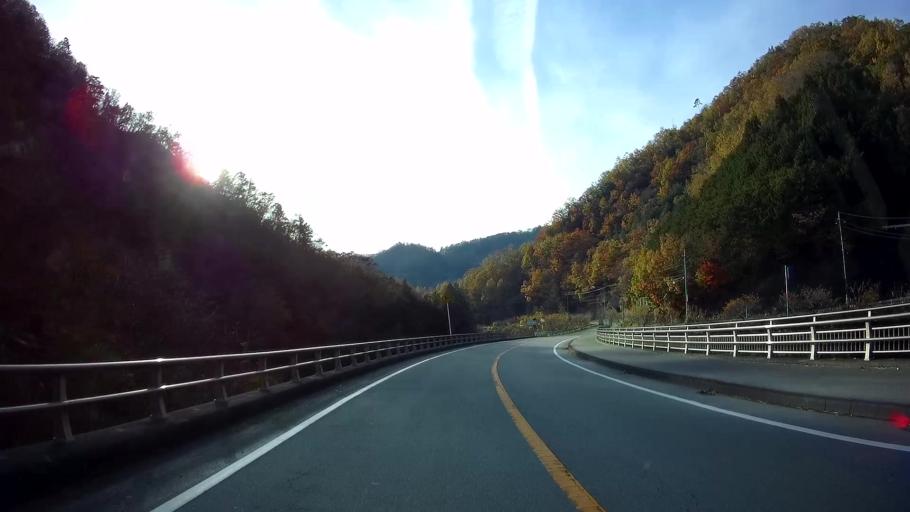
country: JP
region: Yamanashi
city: Fujikawaguchiko
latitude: 35.4708
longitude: 138.5216
